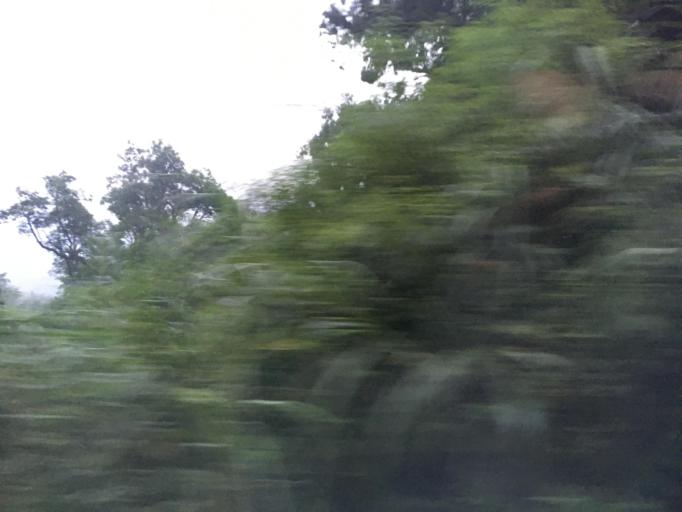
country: TW
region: Taiwan
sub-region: Chiayi
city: Jiayi Shi
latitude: 23.5081
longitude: 120.6595
